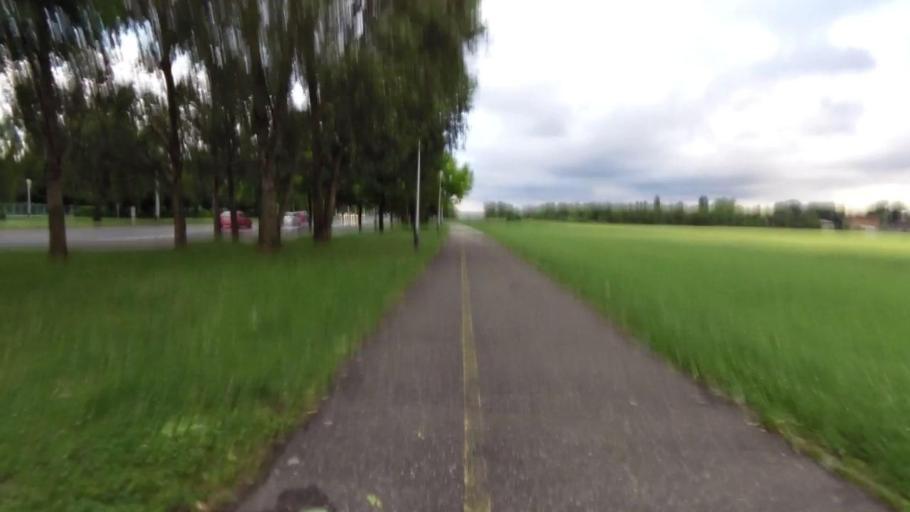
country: HR
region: Grad Zagreb
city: Dubrava
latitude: 45.8333
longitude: 16.0329
